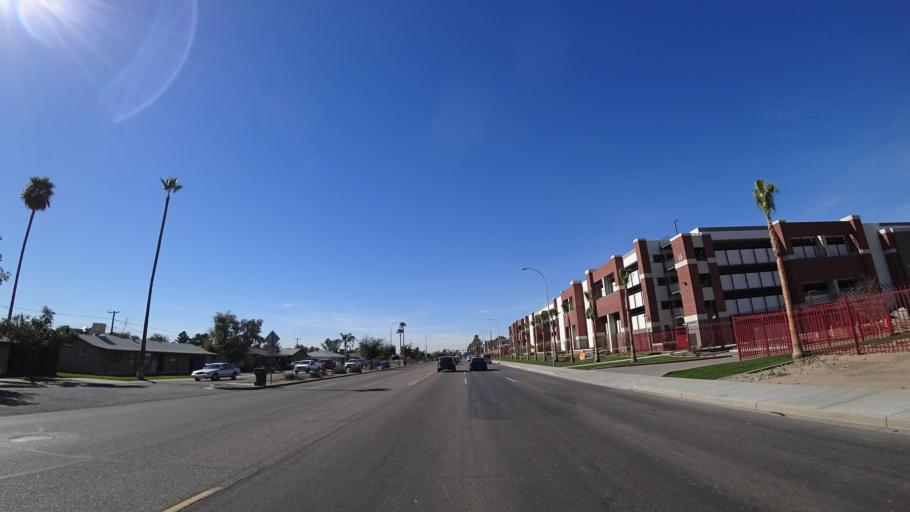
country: US
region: Arizona
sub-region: Maricopa County
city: Glendale
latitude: 33.5095
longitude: -112.1220
